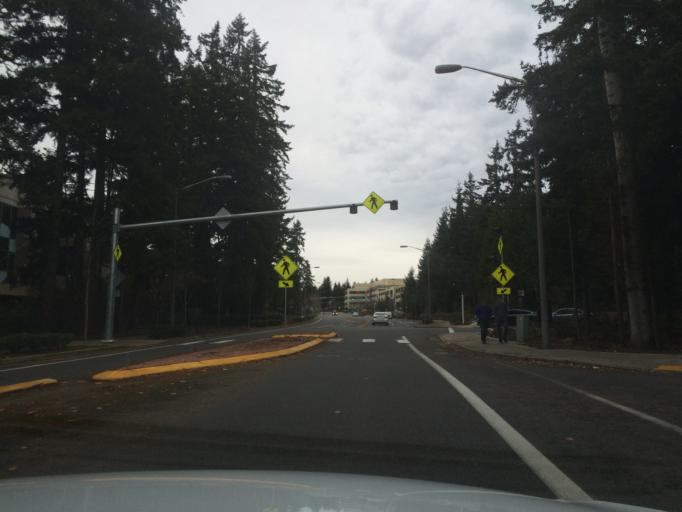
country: US
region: Washington
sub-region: King County
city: Redmond
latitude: 47.6405
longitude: -122.1368
